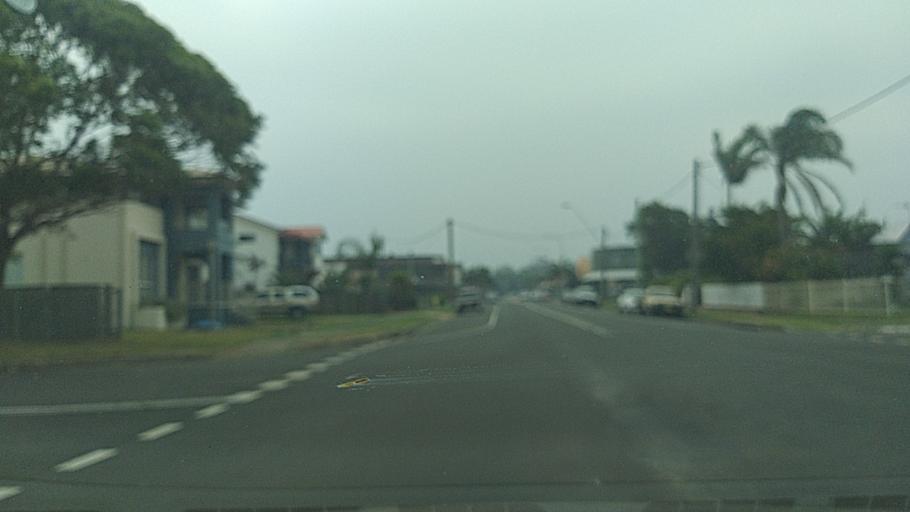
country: AU
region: New South Wales
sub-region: Shellharbour
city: Lake Illawarra
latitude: -34.5528
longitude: 150.8632
